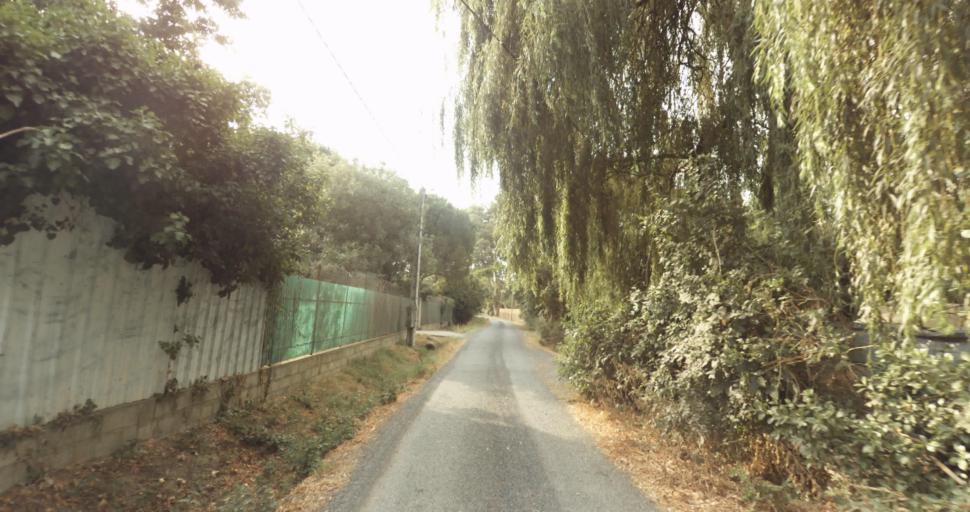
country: FR
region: Languedoc-Roussillon
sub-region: Departement des Pyrenees-Orientales
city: Corneilla-del-Vercol
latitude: 42.6128
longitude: 2.9464
